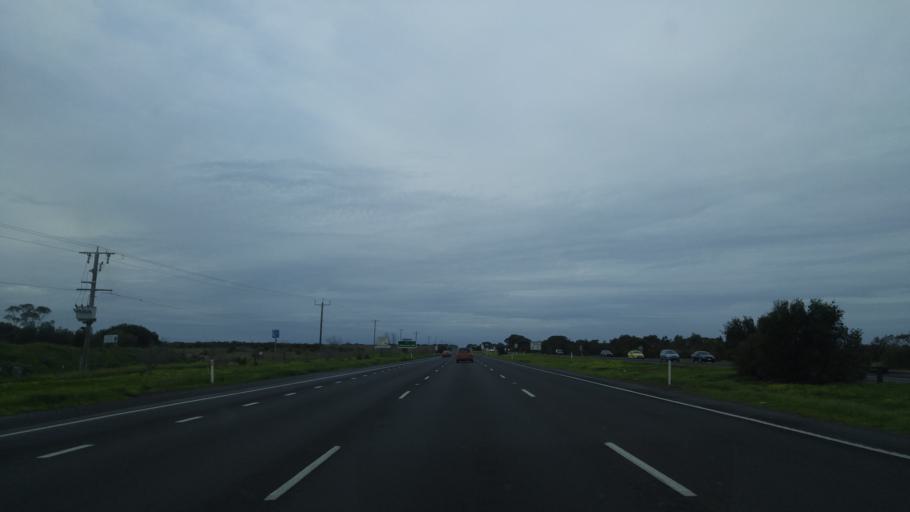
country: AU
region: Victoria
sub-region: Wyndham
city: Little River
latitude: -38.0112
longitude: 144.4720
